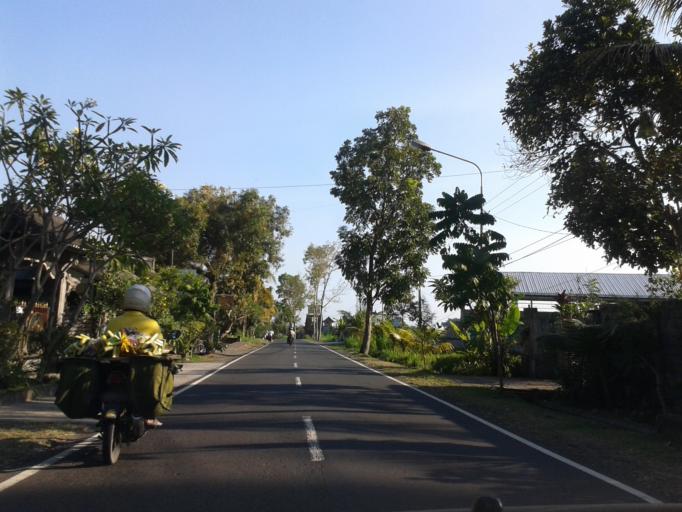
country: ID
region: Bali
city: Banjar Wangsian
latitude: -8.4851
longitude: 115.4012
